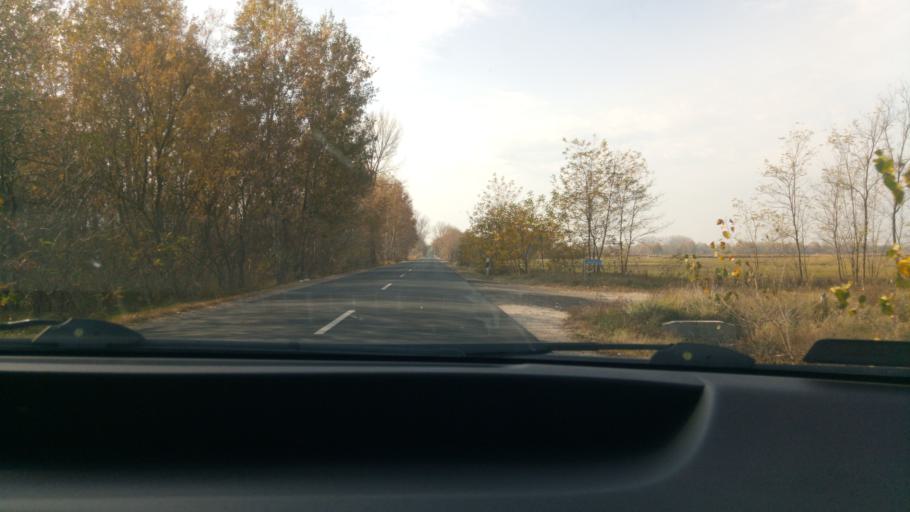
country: HU
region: Bacs-Kiskun
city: Jaszszentlaszlo
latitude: 46.5761
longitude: 19.7681
